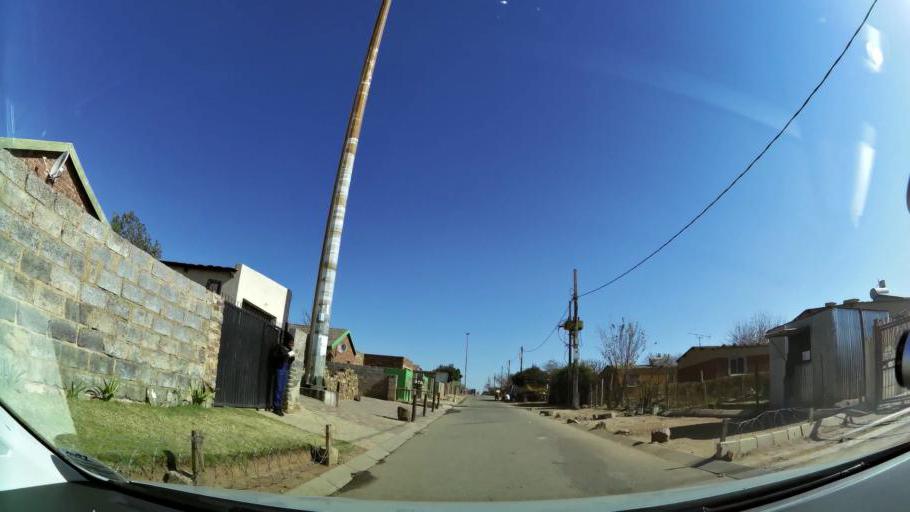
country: ZA
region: Gauteng
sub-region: Ekurhuleni Metropolitan Municipality
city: Tembisa
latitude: -26.0221
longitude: 28.2390
